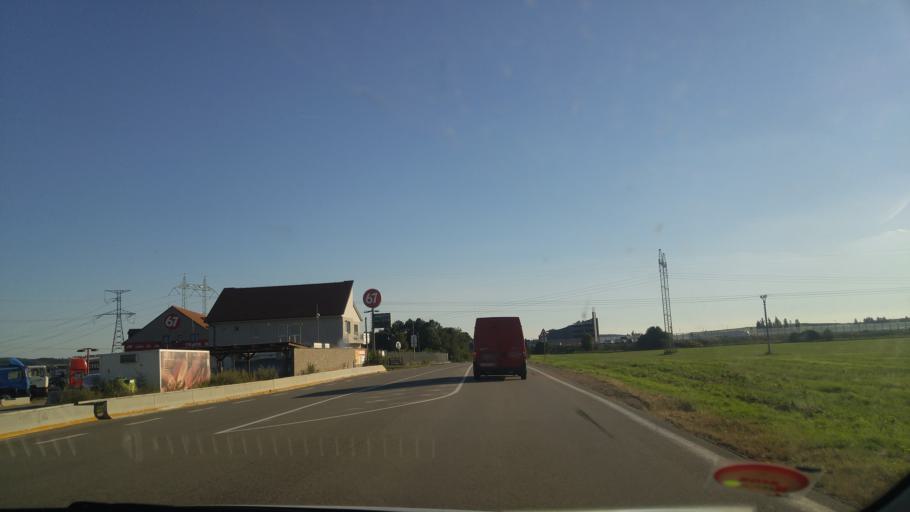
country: CZ
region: South Moravian
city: Ricany
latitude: 49.2192
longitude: 16.4127
